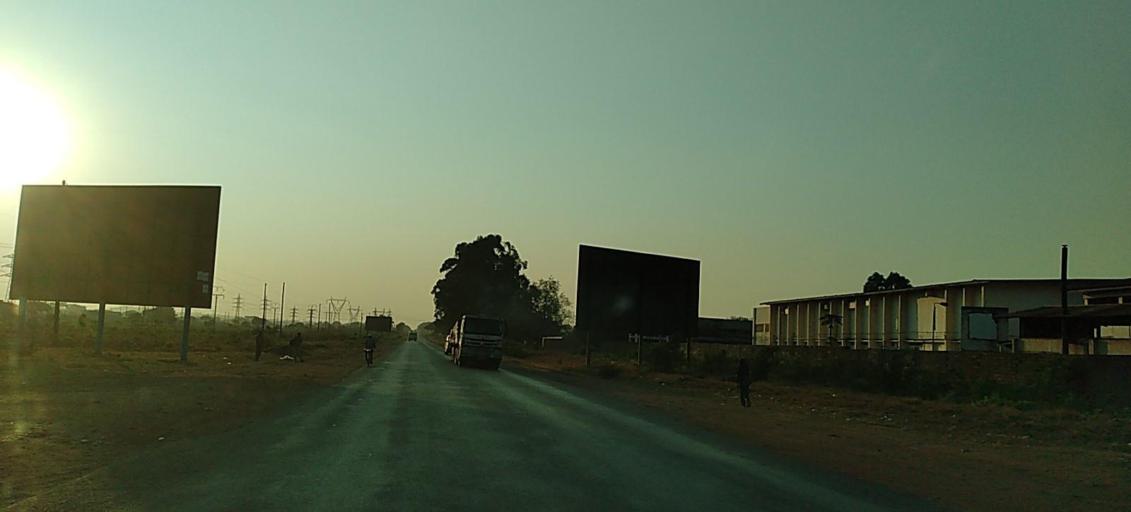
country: ZM
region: Copperbelt
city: Ndola
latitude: -13.0180
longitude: 28.6661
